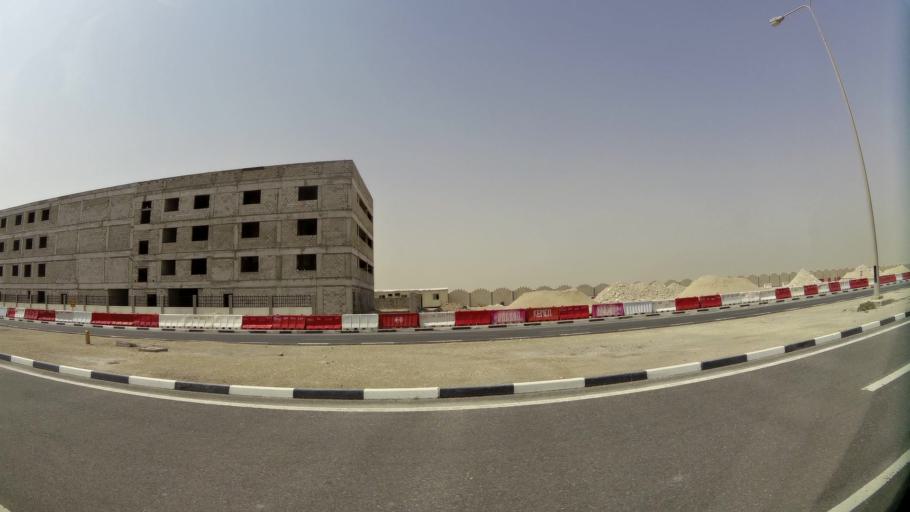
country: QA
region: Al Wakrah
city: Al Wukayr
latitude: 25.1478
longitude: 51.3913
